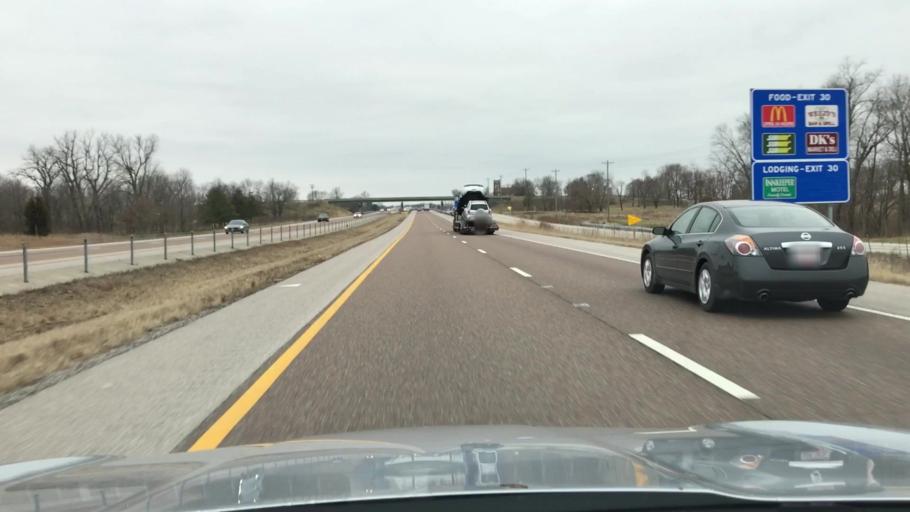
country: US
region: Illinois
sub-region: Madison County
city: Worden
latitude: 38.9138
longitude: -89.8188
